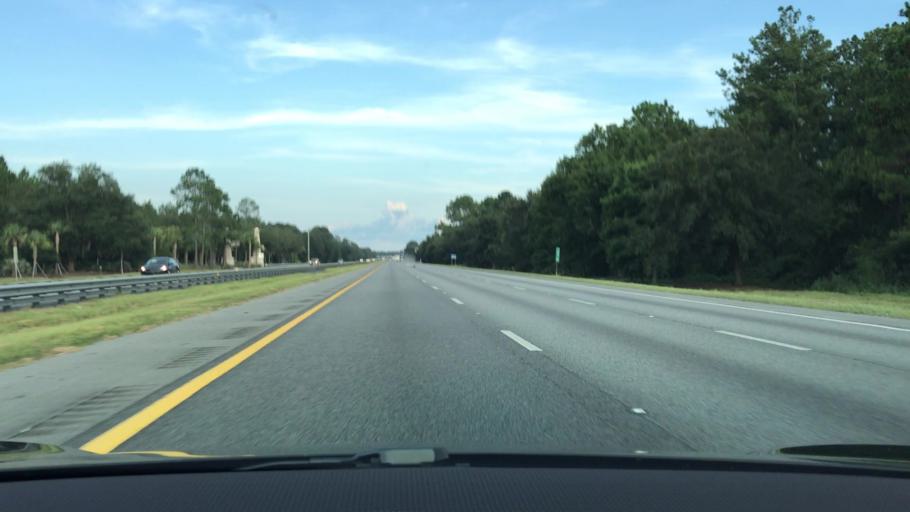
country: US
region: Georgia
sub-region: Echols County
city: Statenville
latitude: 30.6198
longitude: -83.1613
